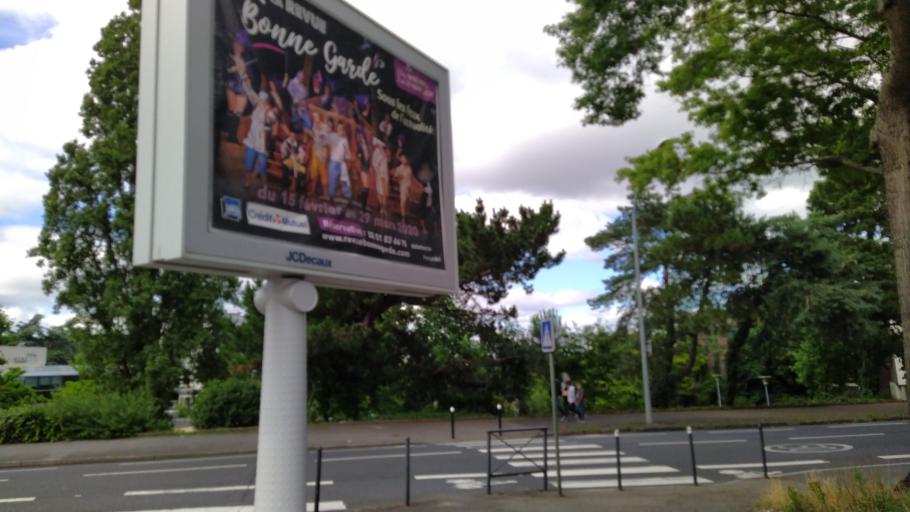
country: FR
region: Pays de la Loire
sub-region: Departement de la Loire-Atlantique
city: Nantes
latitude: 47.2221
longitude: -1.5968
